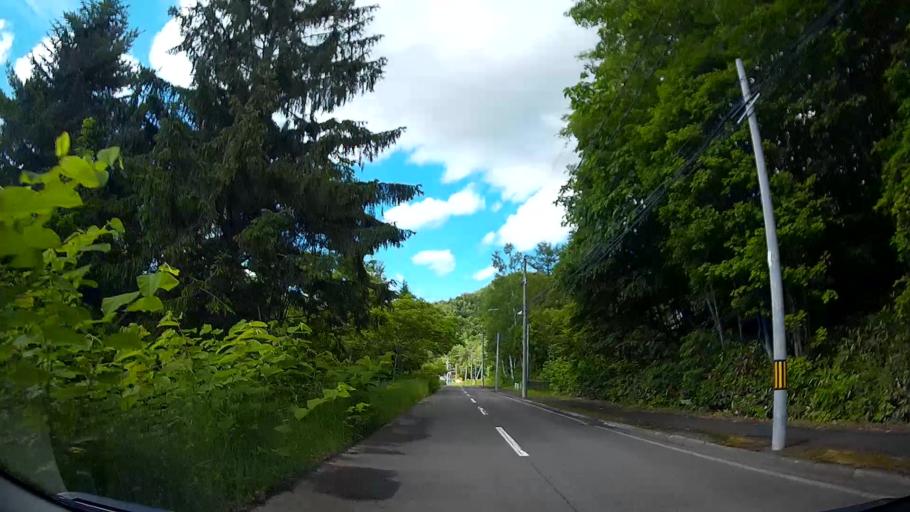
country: JP
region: Hokkaido
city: Sapporo
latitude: 42.9464
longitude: 141.1548
